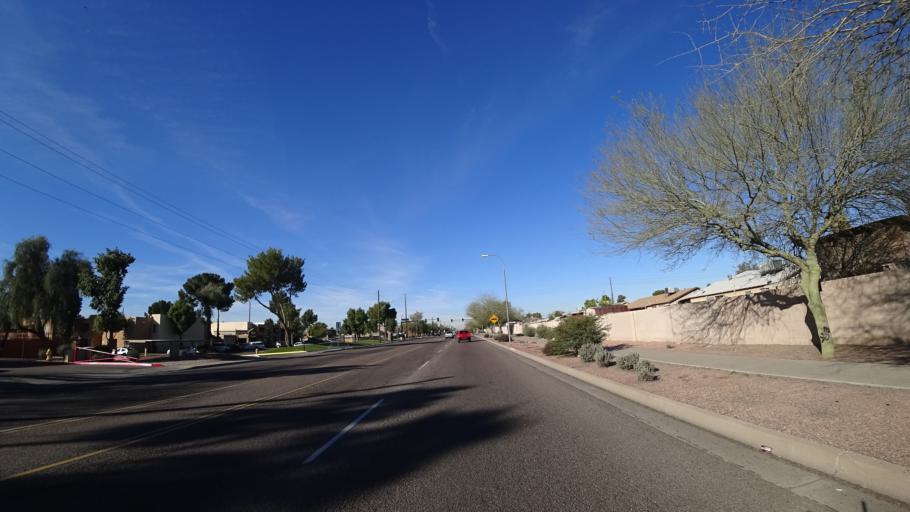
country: US
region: Arizona
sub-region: Maricopa County
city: Tolleson
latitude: 33.4658
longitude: -112.2103
